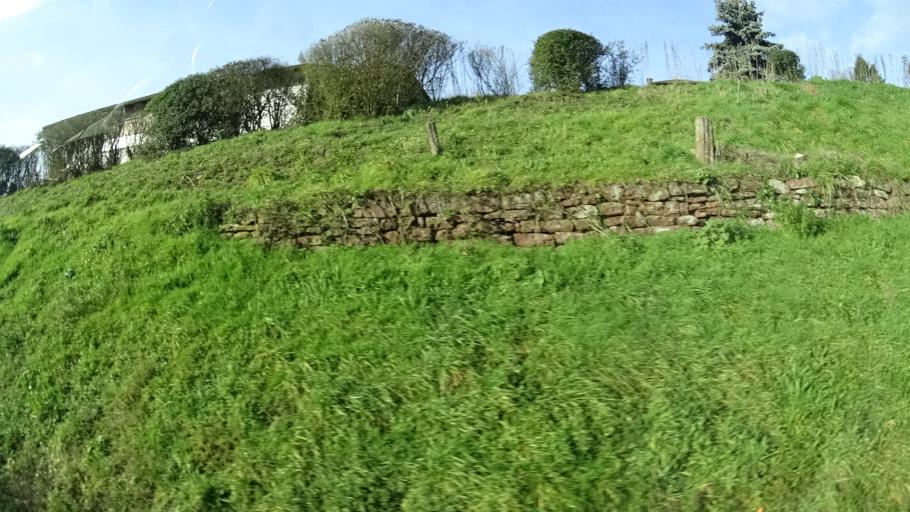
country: DE
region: Bavaria
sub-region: Regierungsbezirk Unterfranken
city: Grossheubach
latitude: 49.7327
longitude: 9.2295
